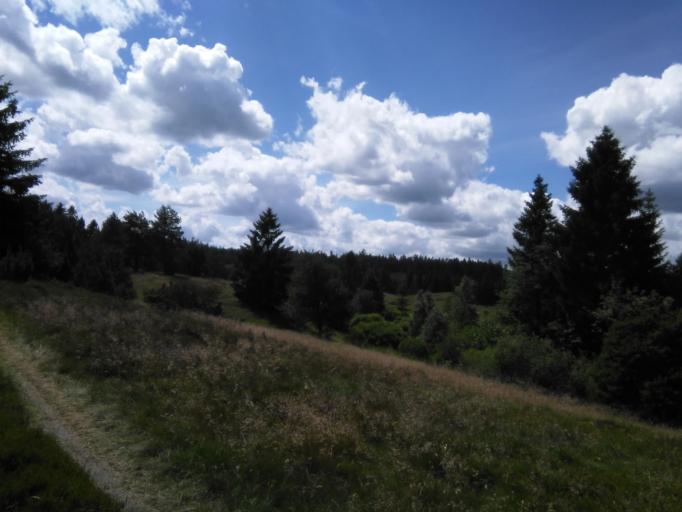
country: DK
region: Central Jutland
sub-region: Silkeborg Kommune
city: Virklund
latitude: 56.0644
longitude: 9.4466
